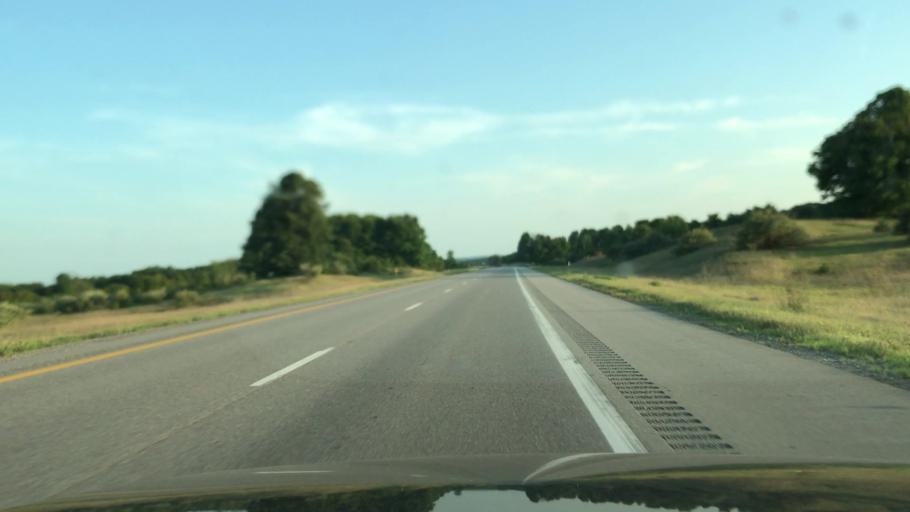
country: US
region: Michigan
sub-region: Osceola County
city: Reed City
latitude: 43.8438
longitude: -85.5328
